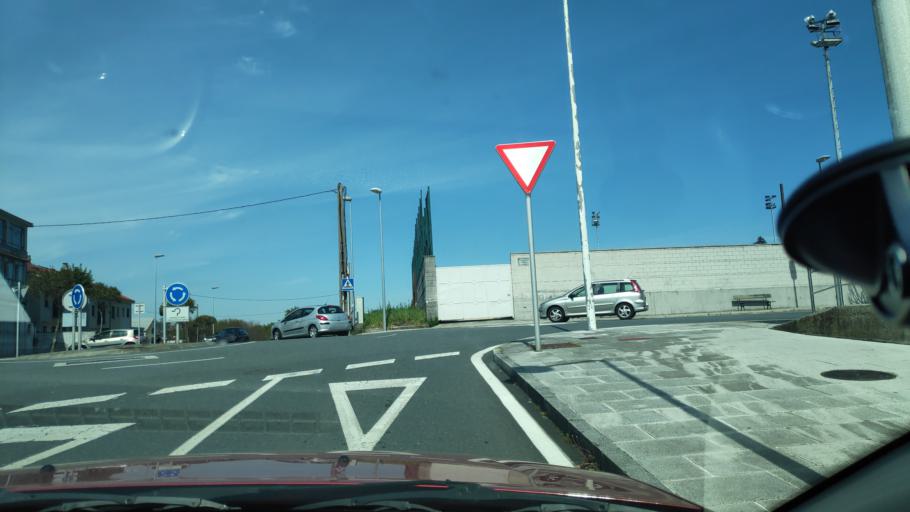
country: ES
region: Galicia
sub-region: Provincia da Coruna
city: Santiago de Compostela
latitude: 42.8910
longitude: -8.5264
